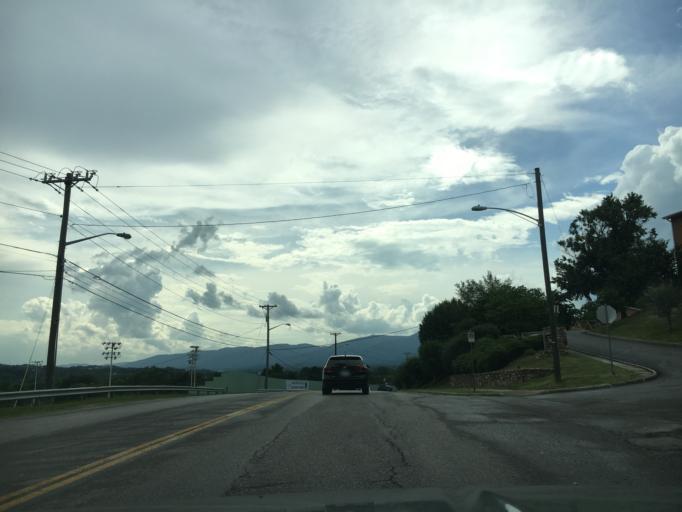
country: US
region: Virginia
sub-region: City of Salem
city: Salem
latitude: 37.2865
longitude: -80.0461
